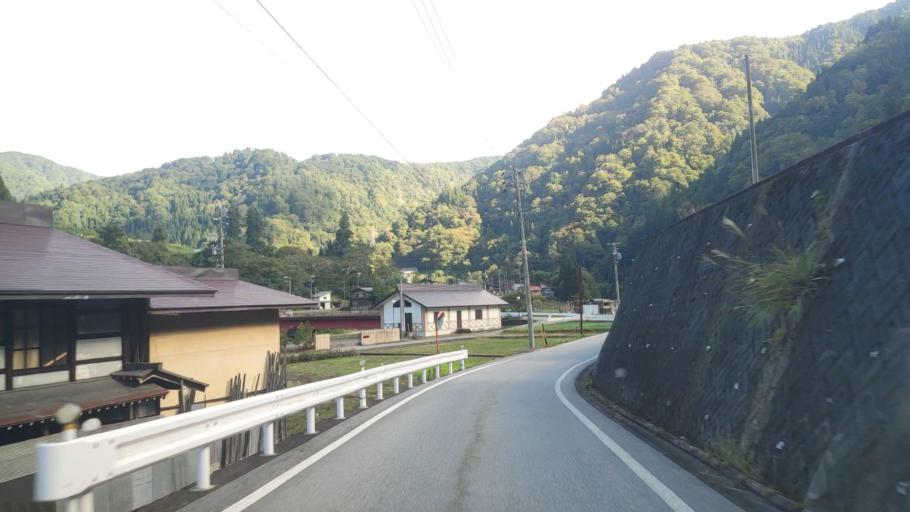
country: JP
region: Gifu
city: Takayama
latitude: 36.2997
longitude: 137.1140
